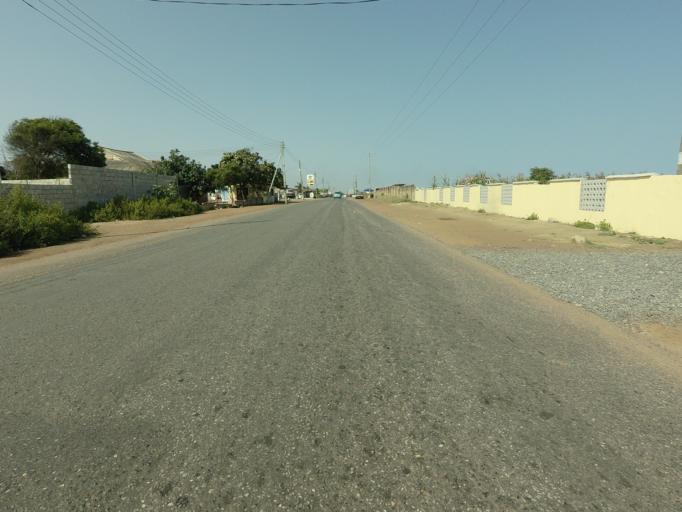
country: GH
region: Greater Accra
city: Teshi Old Town
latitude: 5.5753
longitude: -0.1102
